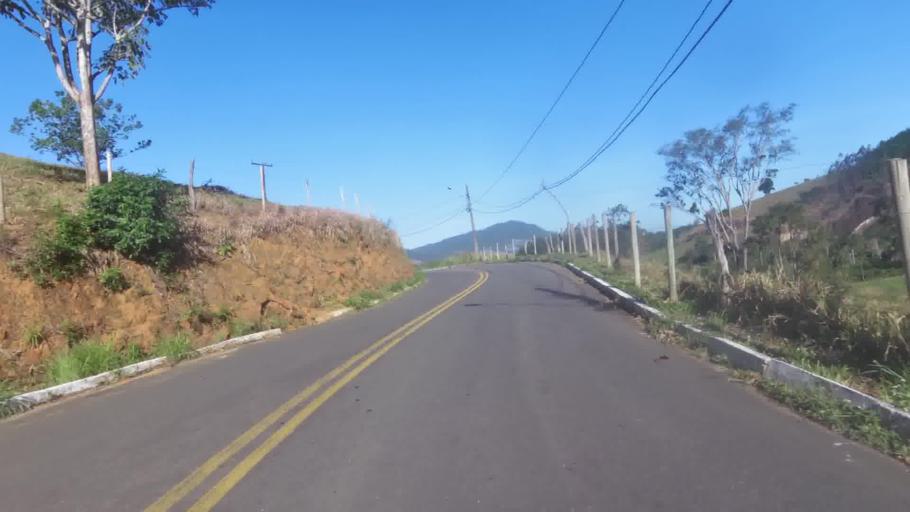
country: BR
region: Espirito Santo
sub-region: Iconha
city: Iconha
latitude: -20.7329
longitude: -40.7811
